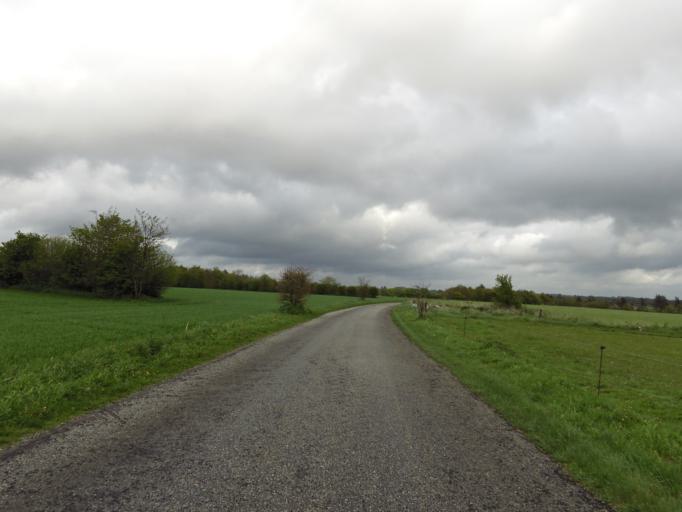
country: DK
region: South Denmark
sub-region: Haderslev Kommune
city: Gram
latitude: 55.2848
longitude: 8.9540
